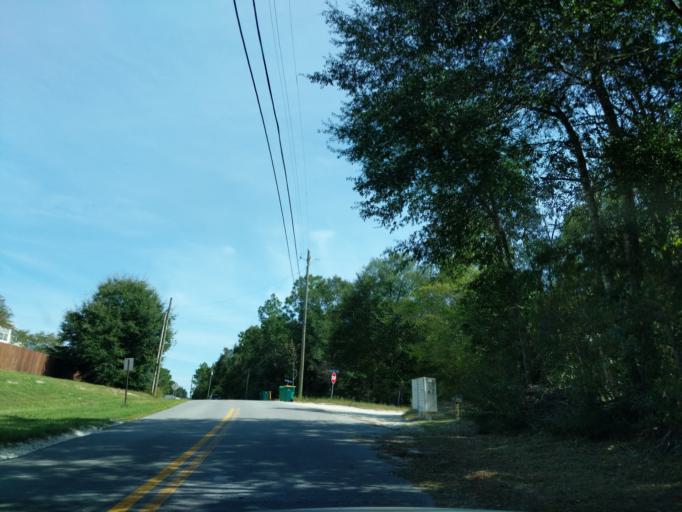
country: US
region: Florida
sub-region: Okaloosa County
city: Crestview
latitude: 30.7058
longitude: -86.5949
